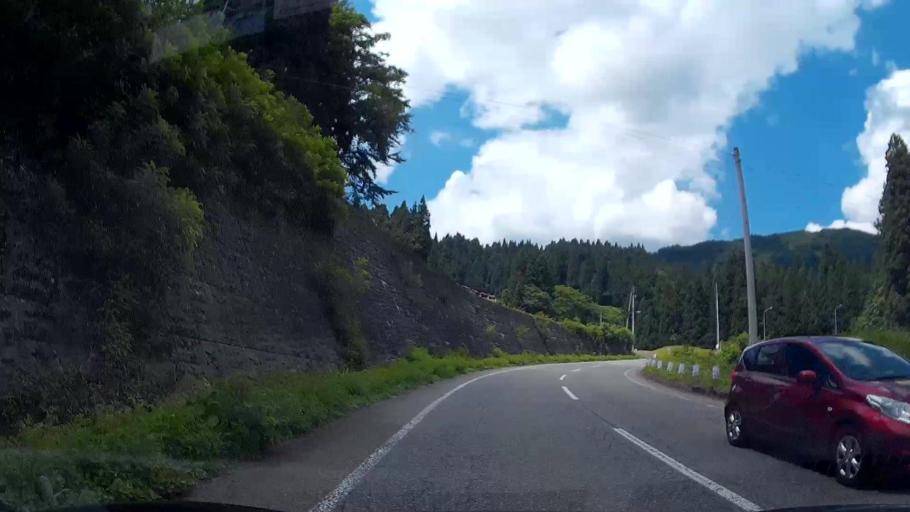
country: JP
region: Niigata
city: Shiozawa
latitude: 37.0227
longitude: 138.8047
